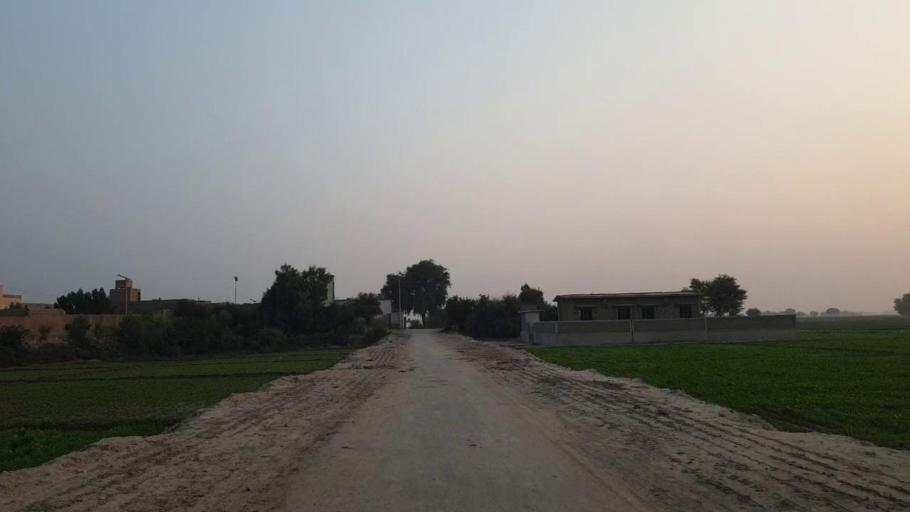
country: PK
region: Sindh
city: Bhan
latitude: 26.5319
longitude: 67.7048
